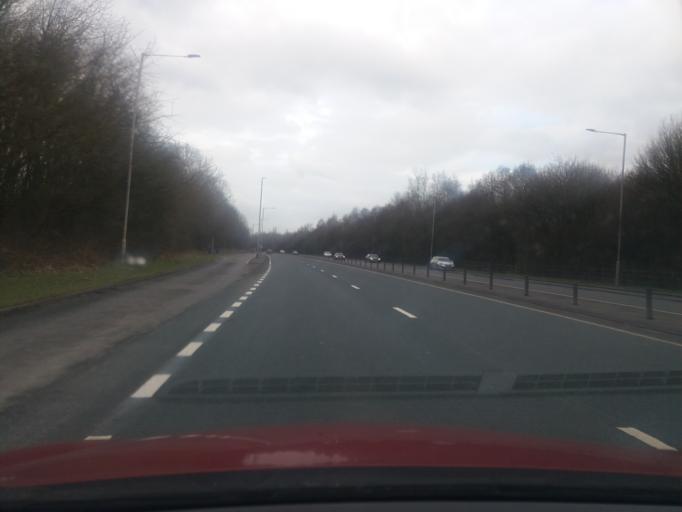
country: GB
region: England
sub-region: Lancashire
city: Leyland
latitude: 53.7376
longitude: -2.6783
